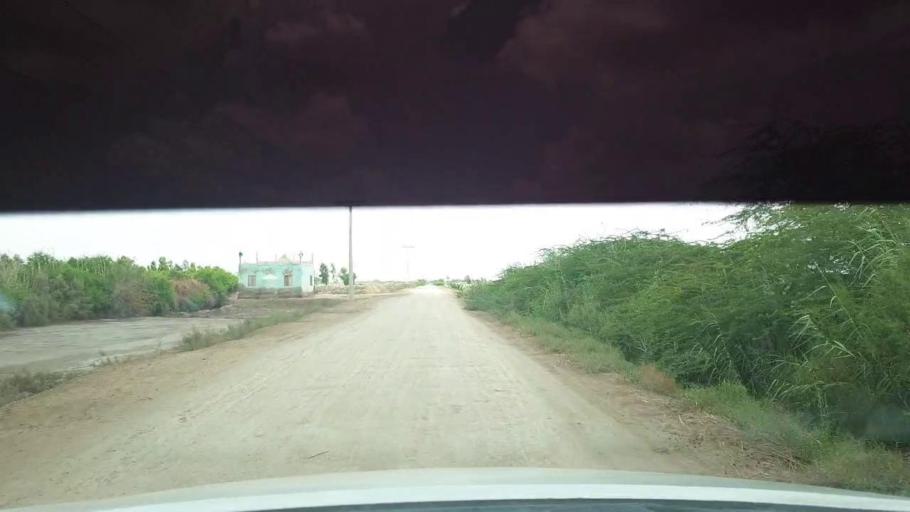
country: PK
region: Sindh
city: Kadhan
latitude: 24.4651
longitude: 68.9966
